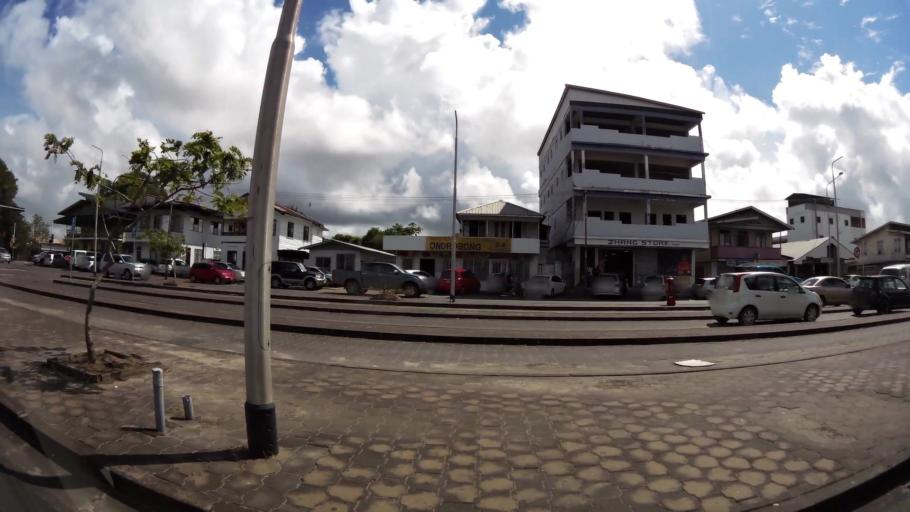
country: SR
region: Paramaribo
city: Paramaribo
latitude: 5.8266
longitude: -55.1660
